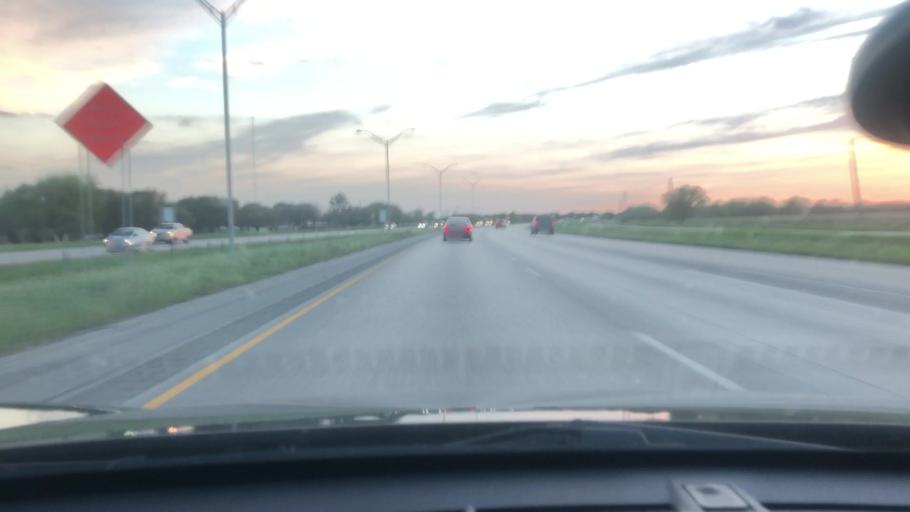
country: US
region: Texas
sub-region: Jackson County
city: Edna
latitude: 28.9648
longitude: -96.6747
